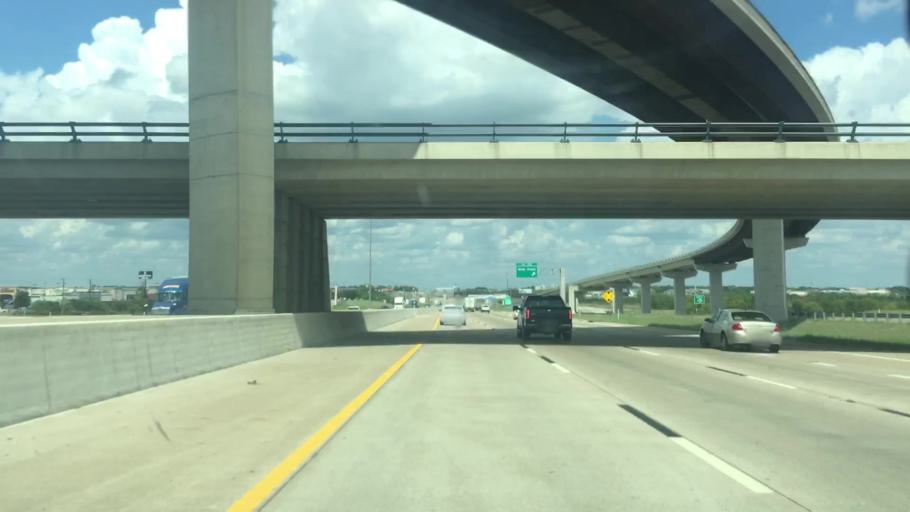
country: US
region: Texas
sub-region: McLennan County
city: Beverly Hills
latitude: 31.4937
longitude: -97.1505
